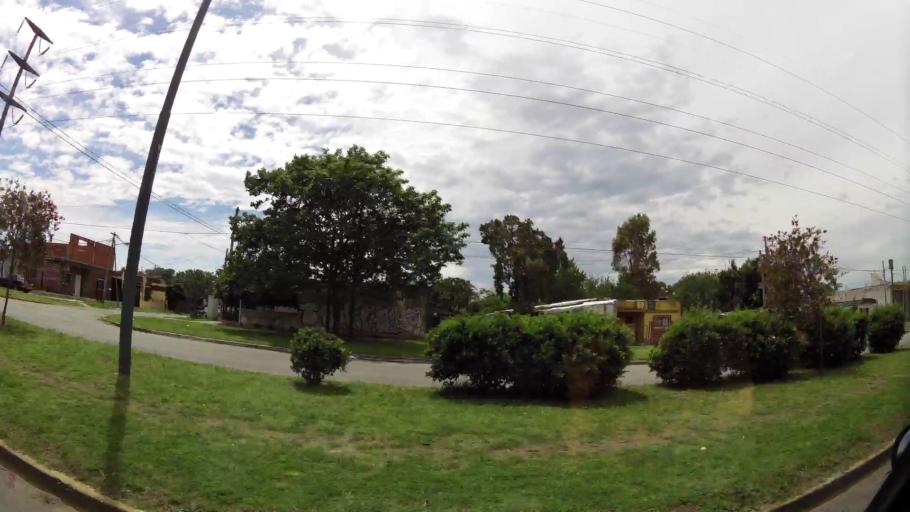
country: AR
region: Buenos Aires
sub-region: Partido de Quilmes
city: Quilmes
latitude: -34.7670
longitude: -58.2339
